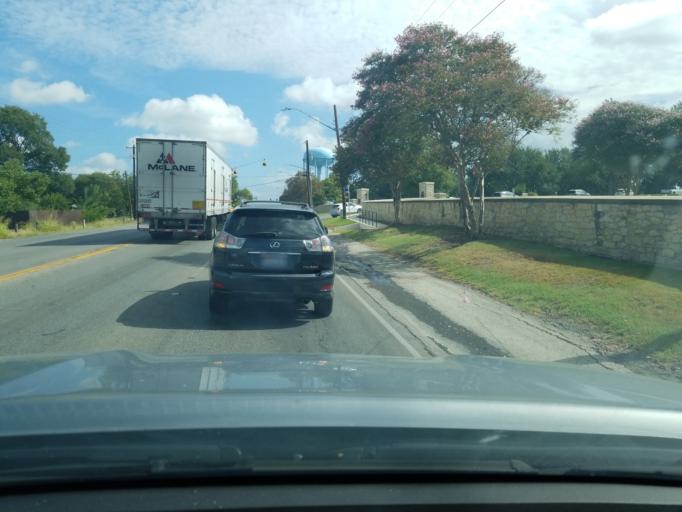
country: US
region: Texas
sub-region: Bexar County
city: Terrell Hills
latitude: 29.4763
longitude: -98.4346
